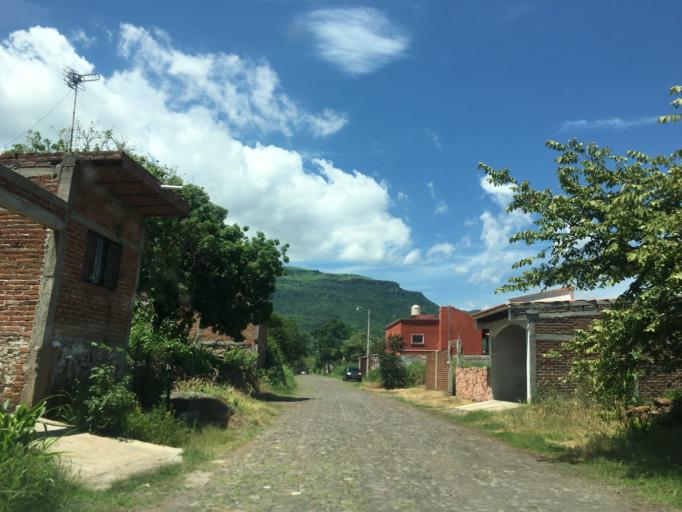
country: MX
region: Nayarit
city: Ixtlan del Rio
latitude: 21.0348
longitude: -104.3510
